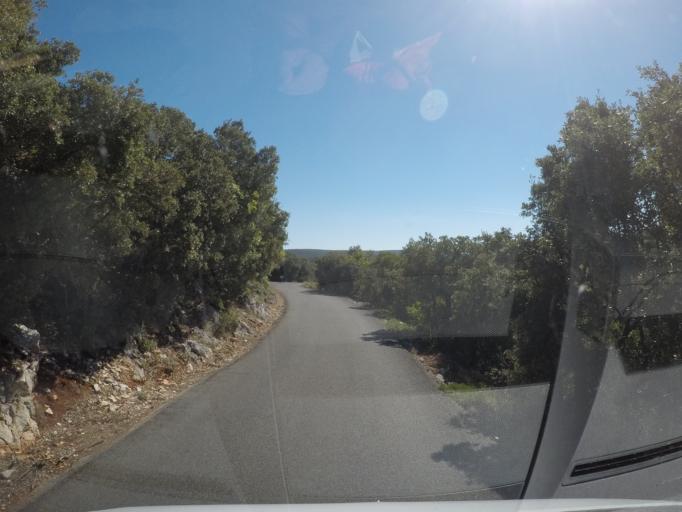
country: FR
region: Languedoc-Roussillon
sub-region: Departement de l'Herault
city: Vailhauques
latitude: 43.7134
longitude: 3.6816
